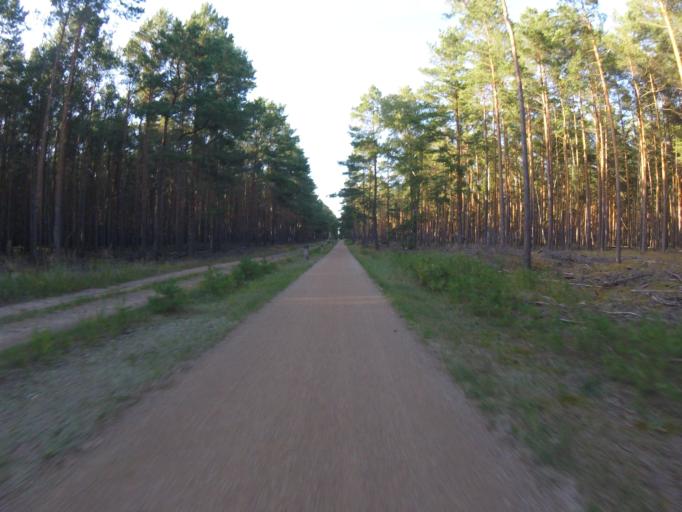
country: DE
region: Brandenburg
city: Munchehofe
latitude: 52.2017
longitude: 13.7667
